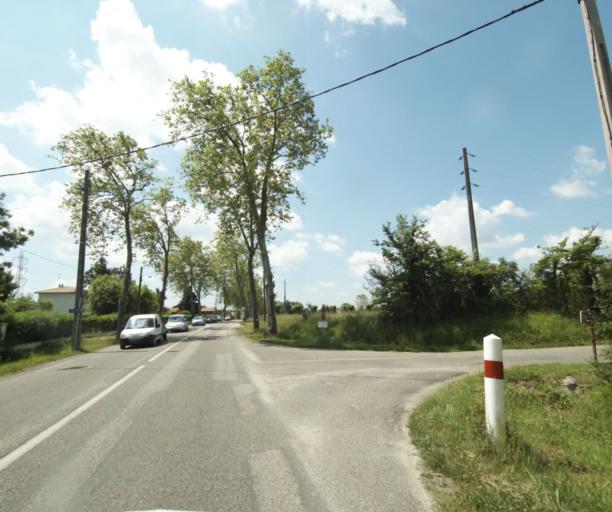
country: FR
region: Midi-Pyrenees
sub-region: Departement du Tarn-et-Garonne
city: Montauban
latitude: 44.0505
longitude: 1.3589
